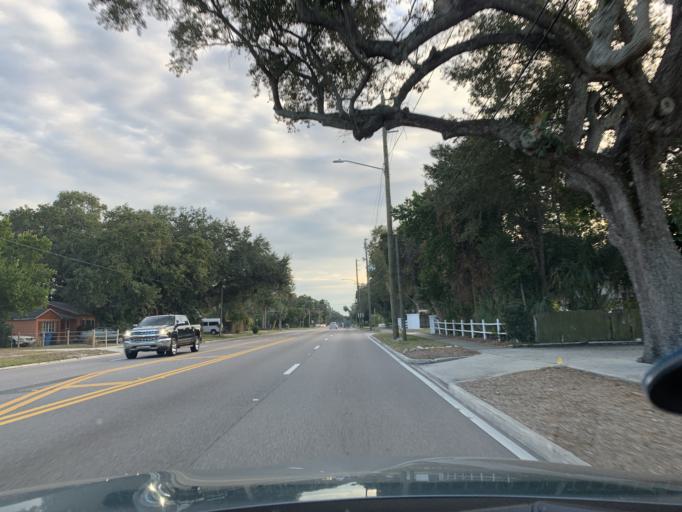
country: US
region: Florida
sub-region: Pinellas County
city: Bay Pines
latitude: 27.8045
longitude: -82.7539
